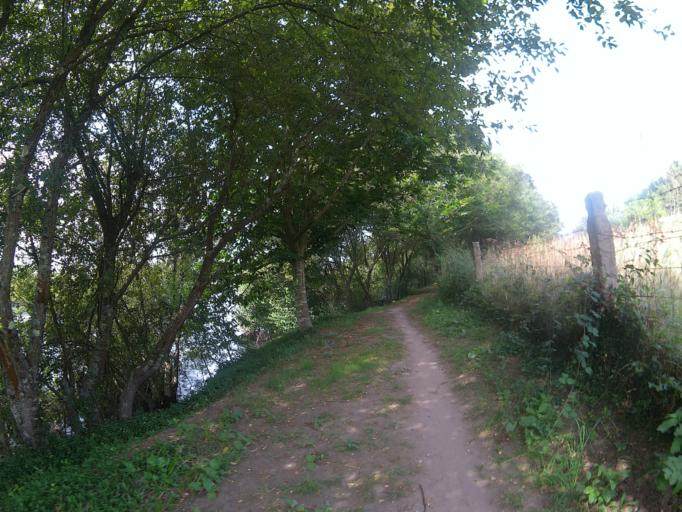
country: PT
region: Viana do Castelo
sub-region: Ponte de Lima
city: Ponte de Lima
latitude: 41.7786
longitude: -8.5723
